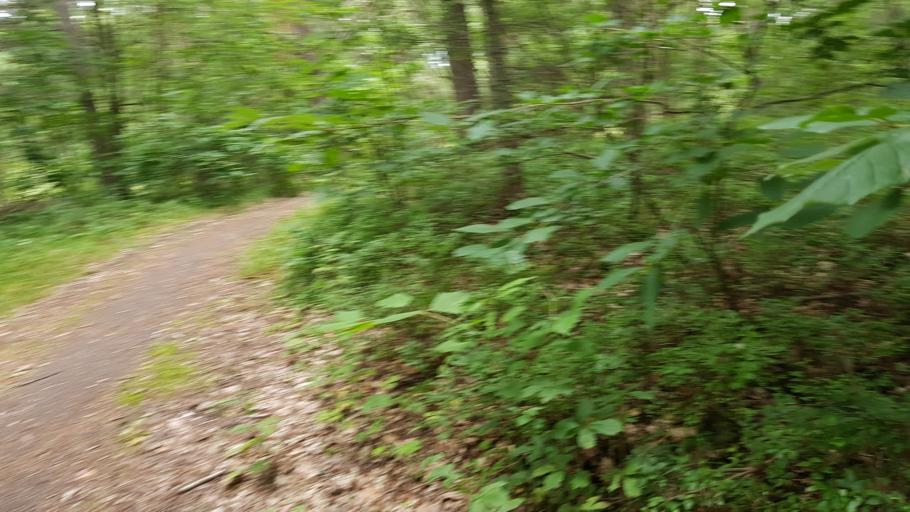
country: SE
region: OEstergoetland
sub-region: Norrkopings Kommun
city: Norrkoping
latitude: 58.5683
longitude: 16.1905
